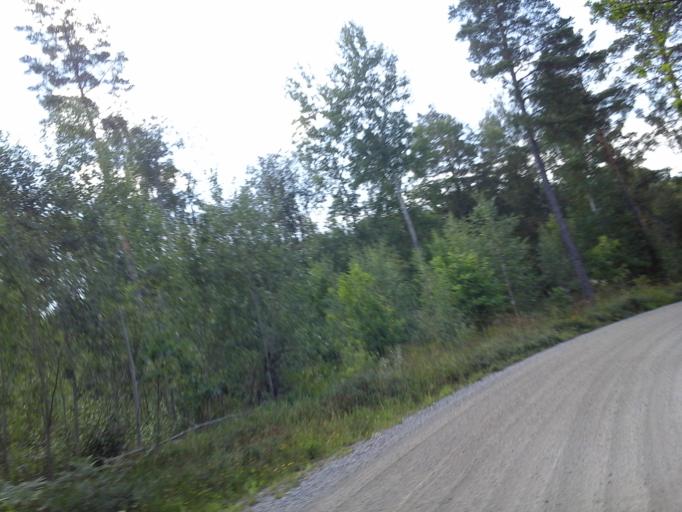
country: SE
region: Soedermanland
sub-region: Eskilstuna Kommun
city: Arla
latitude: 59.2415
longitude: 16.7708
